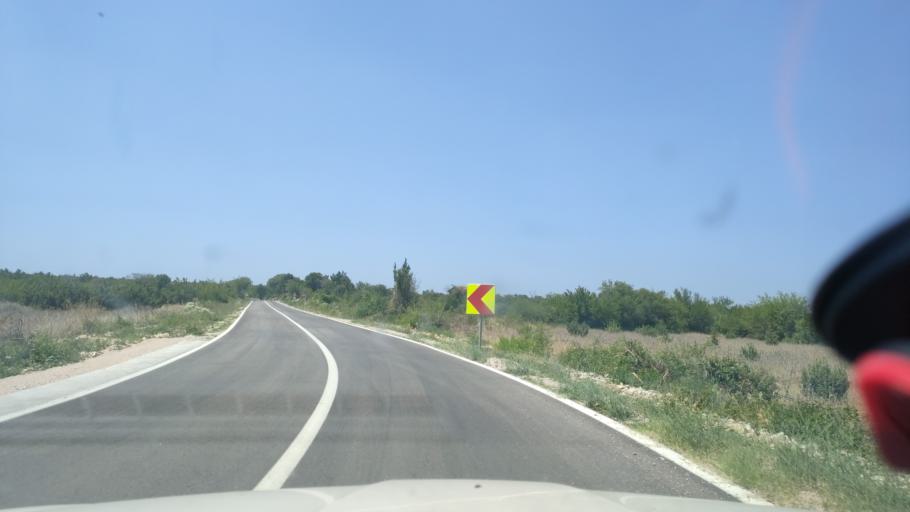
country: HR
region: Sibensko-Kniniska
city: Kistanje
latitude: 43.9776
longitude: 15.9443
